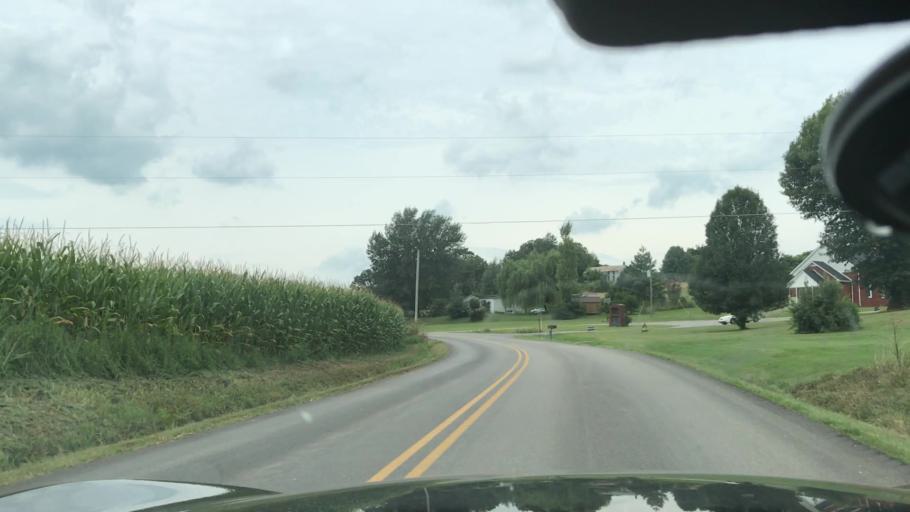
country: US
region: Kentucky
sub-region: Hart County
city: Munfordville
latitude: 37.2335
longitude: -85.7018
